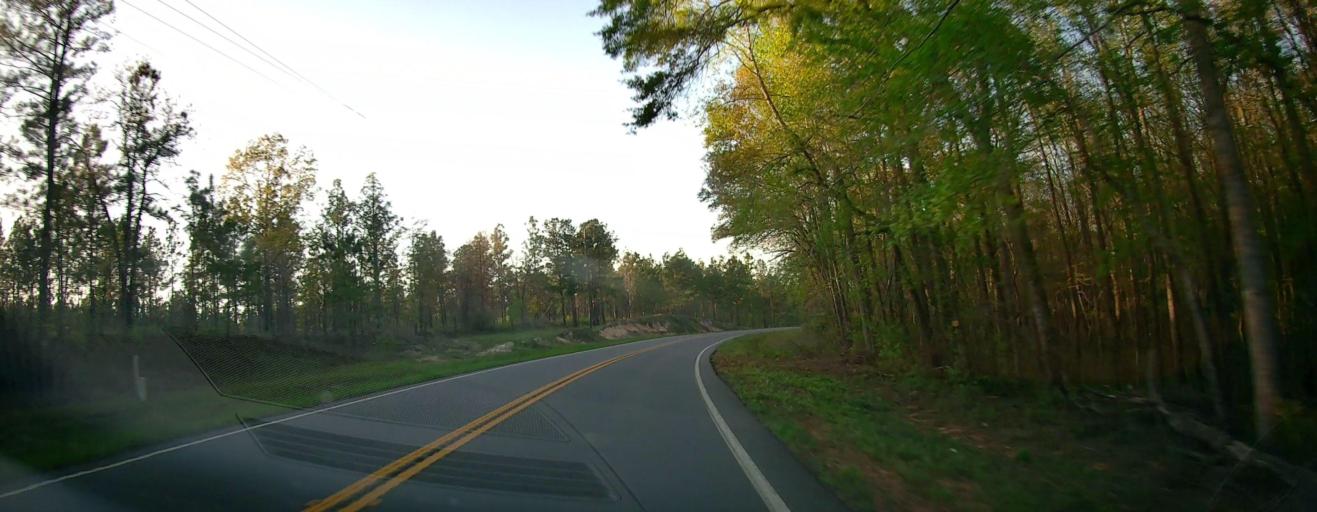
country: US
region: Georgia
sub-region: Talbot County
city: Talbotton
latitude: 32.5603
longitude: -84.5424
